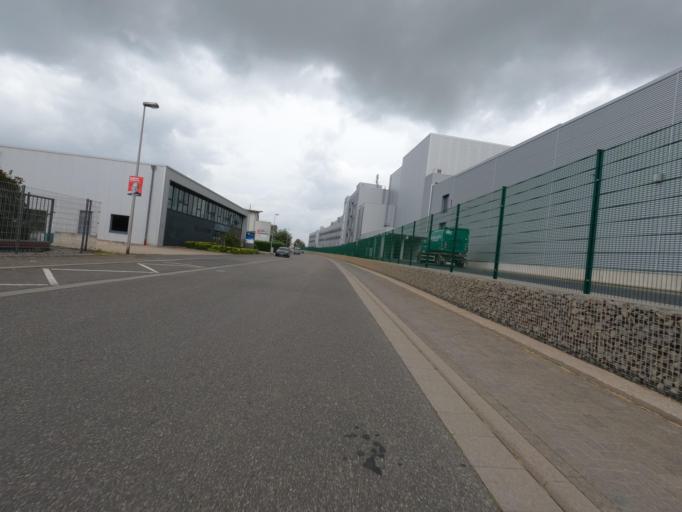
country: DE
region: North Rhine-Westphalia
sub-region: Regierungsbezirk Koln
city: Ubach-Palenberg
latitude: 50.9151
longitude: 6.1461
